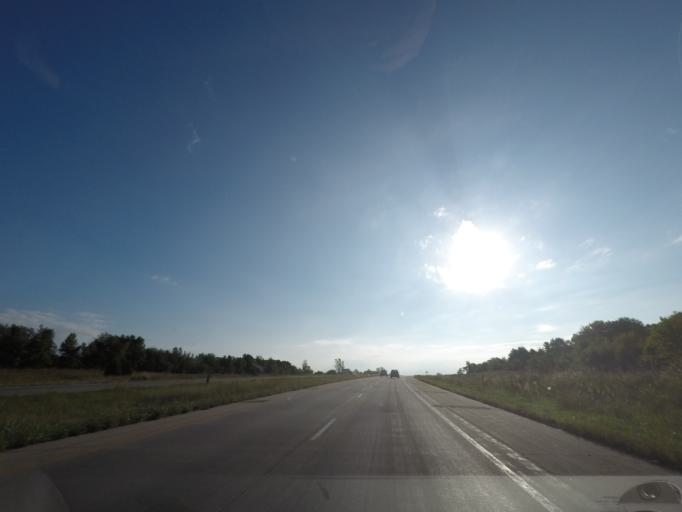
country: US
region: Iowa
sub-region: Warren County
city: Carlisle
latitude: 41.5117
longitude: -93.5477
